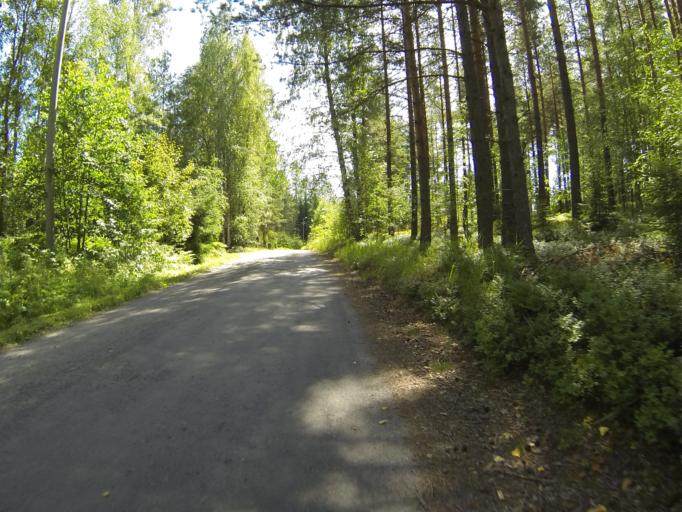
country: FI
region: Varsinais-Suomi
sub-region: Salo
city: Saerkisalo
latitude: 60.2621
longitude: 22.9736
